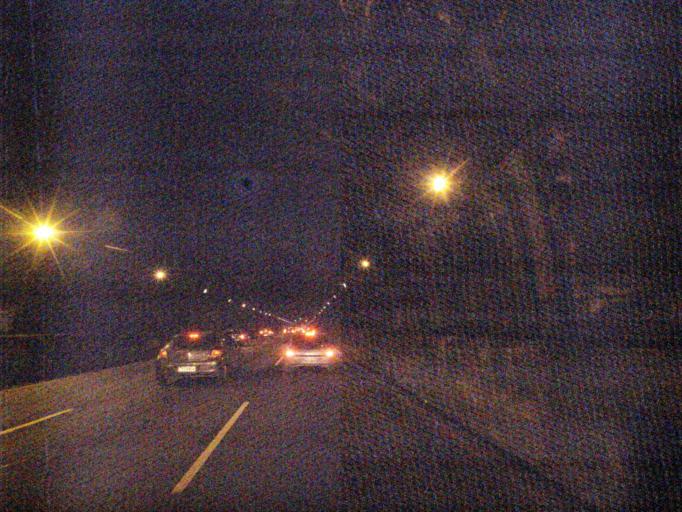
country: BR
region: Rio de Janeiro
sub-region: Rio De Janeiro
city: Rio de Janeiro
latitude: -22.9427
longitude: -43.2026
